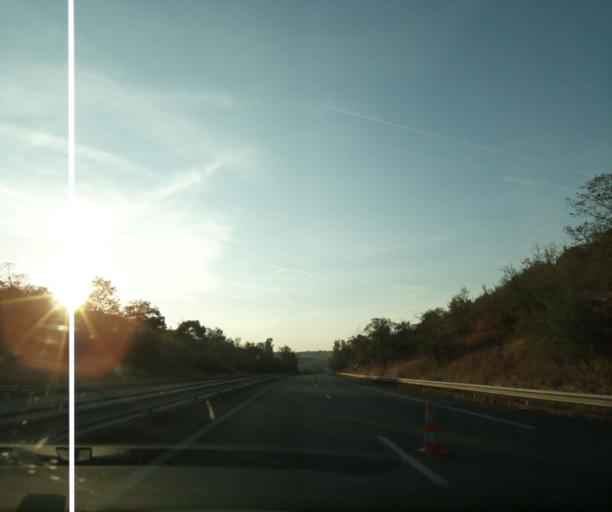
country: FR
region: Midi-Pyrenees
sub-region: Departement du Tarn-et-Garonne
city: Auvillar
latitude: 44.0569
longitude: 0.8749
